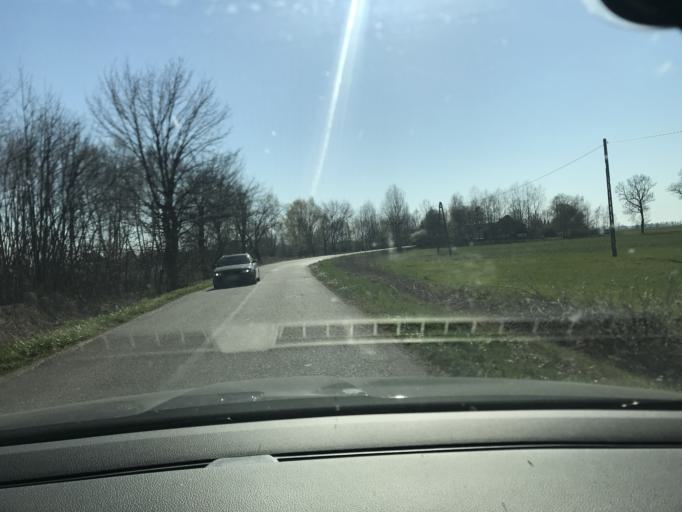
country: PL
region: Pomeranian Voivodeship
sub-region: Powiat nowodworski
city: Sztutowo
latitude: 54.2996
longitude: 19.1470
